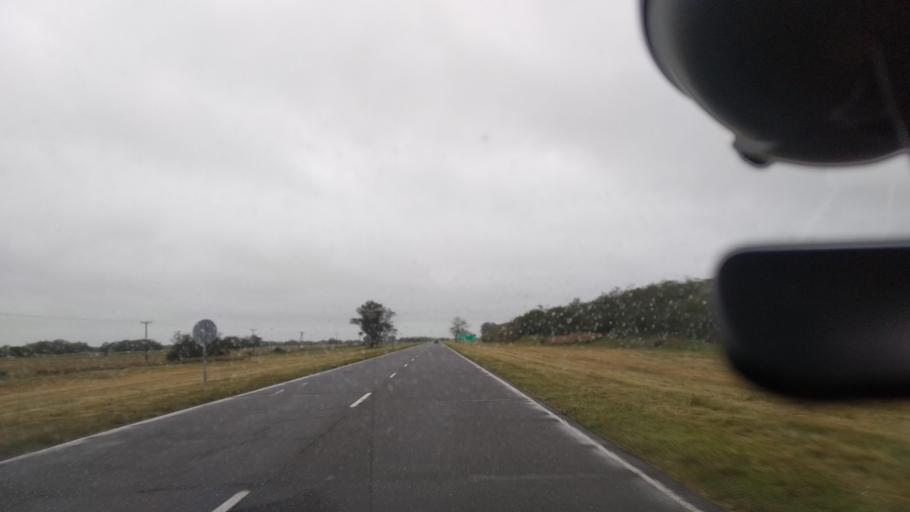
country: AR
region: Buenos Aires
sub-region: Partido de Castelli
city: Castelli
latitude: -36.0346
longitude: -57.4469
